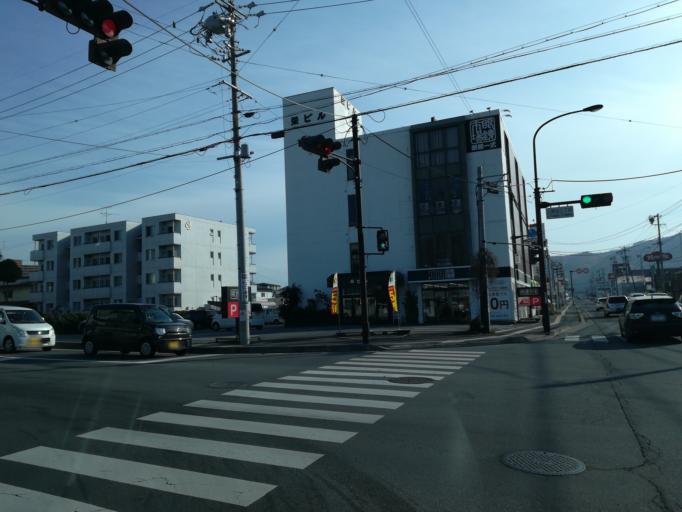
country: JP
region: Nagano
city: Ueda
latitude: 36.3944
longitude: 138.2661
